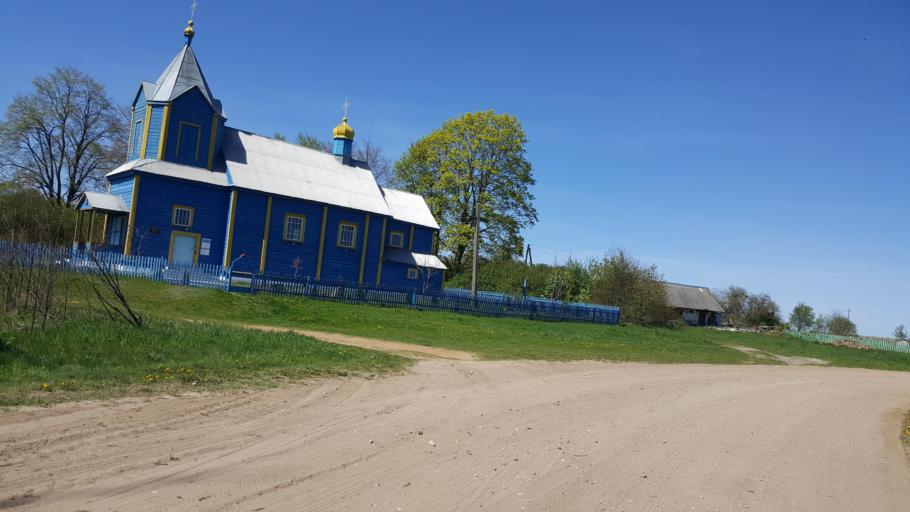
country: BY
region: Brest
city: Kamyanyets
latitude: 52.4542
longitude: 23.8741
